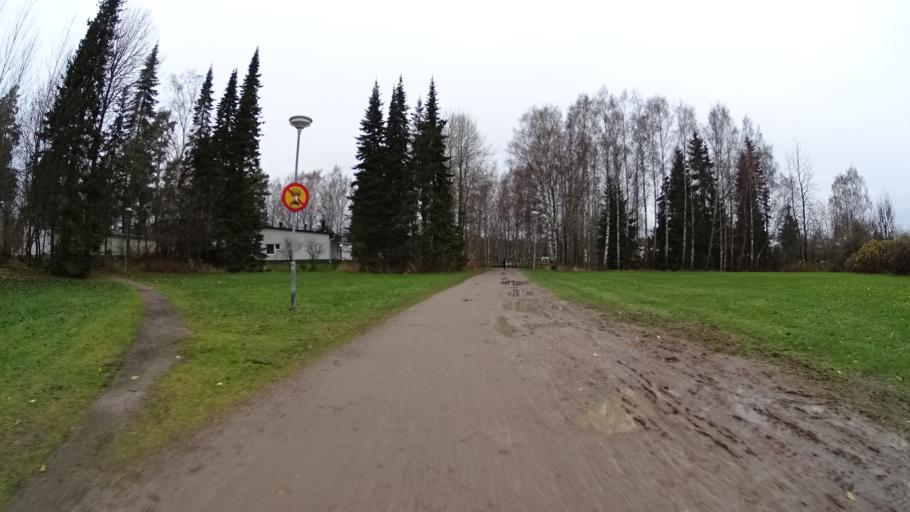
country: FI
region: Uusimaa
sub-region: Helsinki
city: Otaniemi
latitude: 60.1821
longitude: 24.7989
